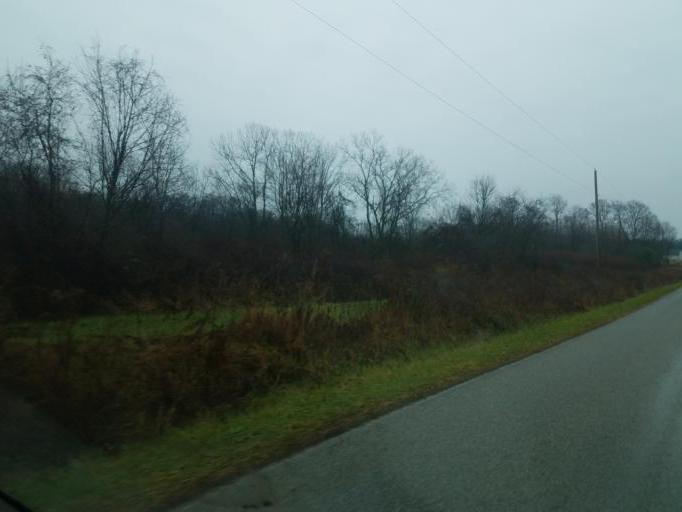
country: US
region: Ohio
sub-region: Knox County
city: Centerburg
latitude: 40.3622
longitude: -82.6880
